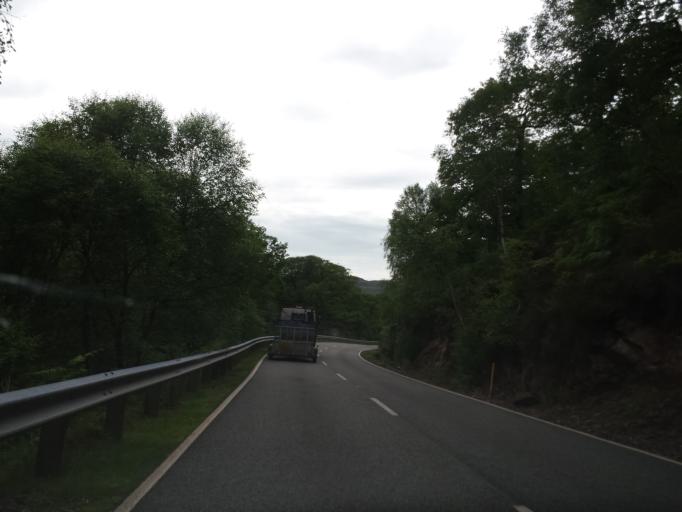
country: GB
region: Scotland
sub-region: Argyll and Bute
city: Isle Of Mull
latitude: 56.8998
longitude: -5.7712
